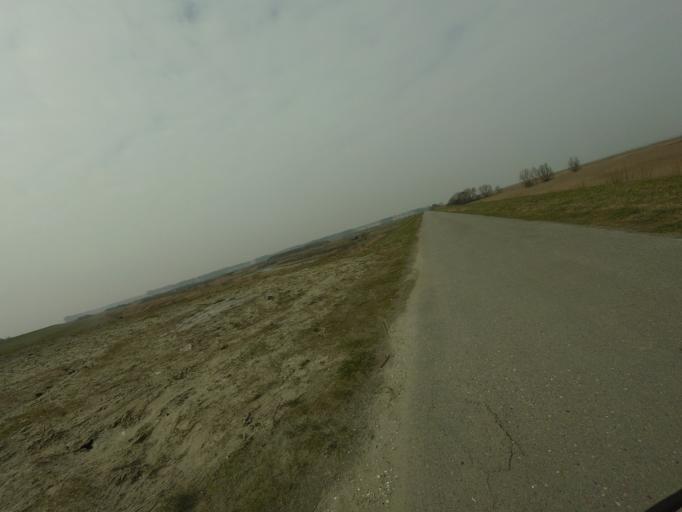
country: NL
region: North Brabant
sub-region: Gemeente Woensdrecht
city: Woensdrecht
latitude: 51.3380
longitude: 4.2439
